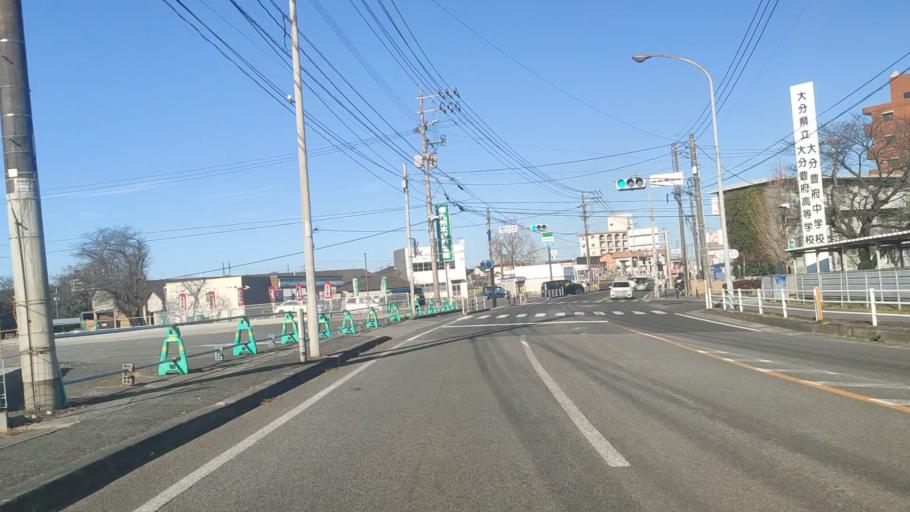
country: JP
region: Oita
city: Oita
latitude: 33.2067
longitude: 131.6035
